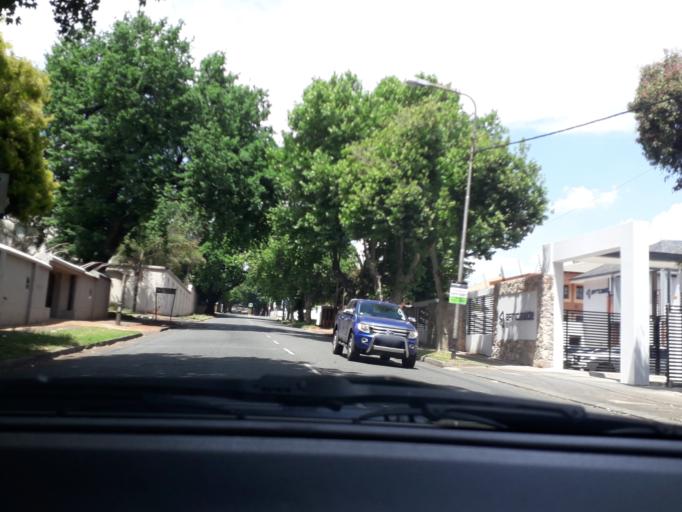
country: ZA
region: Gauteng
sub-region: City of Johannesburg Metropolitan Municipality
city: Johannesburg
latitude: -26.1668
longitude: 28.0566
